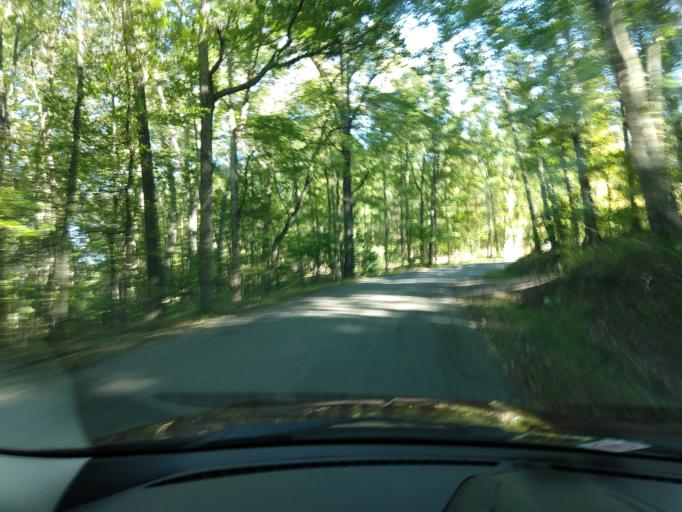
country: US
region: Virginia
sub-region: Alleghany County
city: Clifton Forge
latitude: 37.8496
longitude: -79.8474
